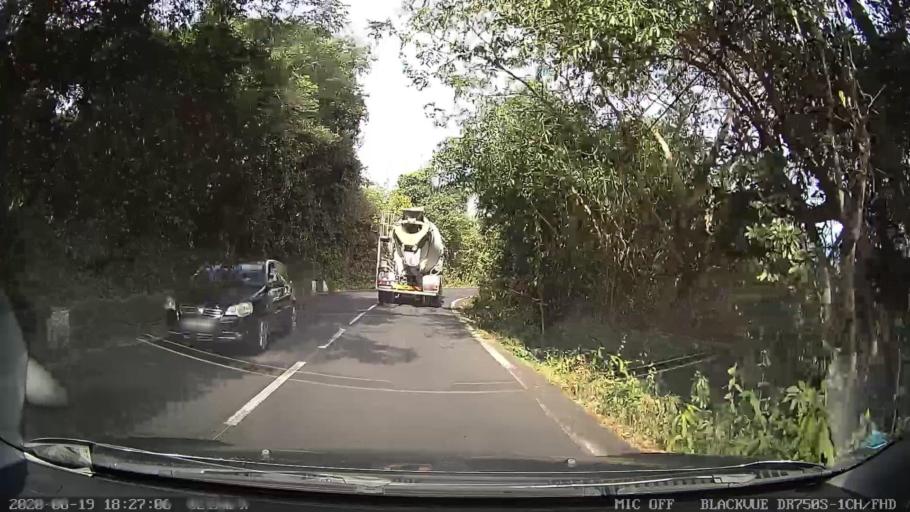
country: RE
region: Reunion
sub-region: Reunion
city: La Possession
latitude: -20.9549
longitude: 55.3511
